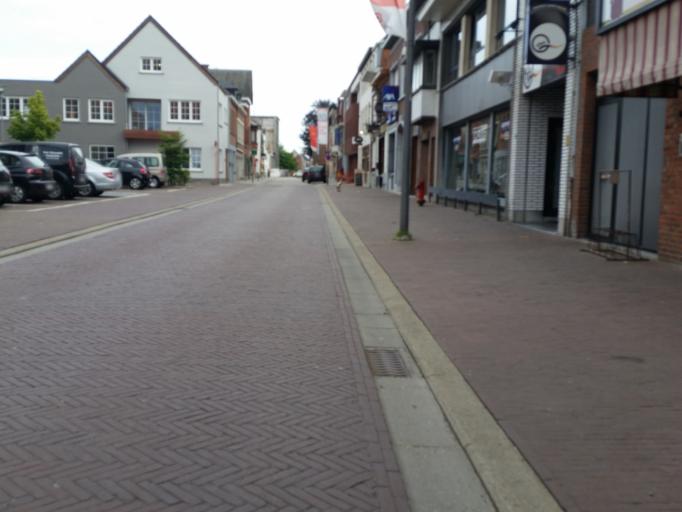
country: BE
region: Flanders
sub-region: Provincie Antwerpen
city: Willebroek
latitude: 51.0445
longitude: 4.3257
